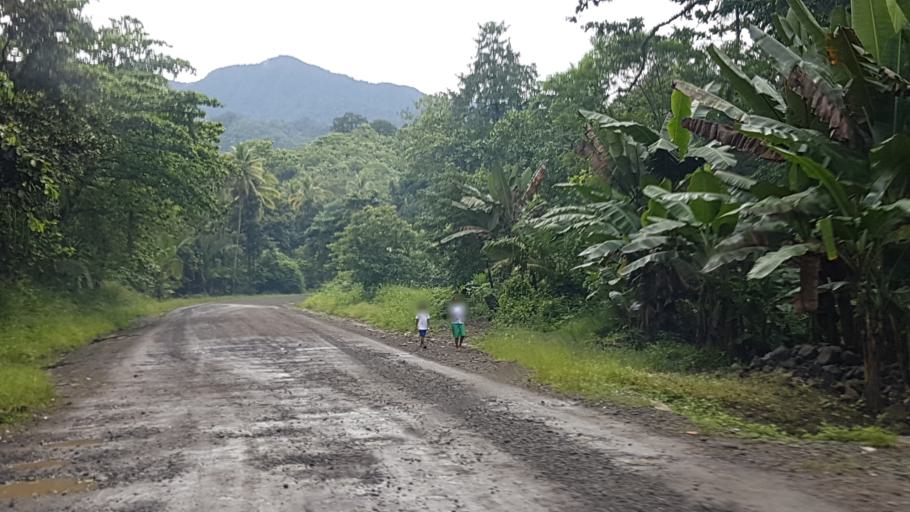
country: PG
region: Milne Bay
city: Alotau
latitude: -10.3256
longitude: 150.5025
